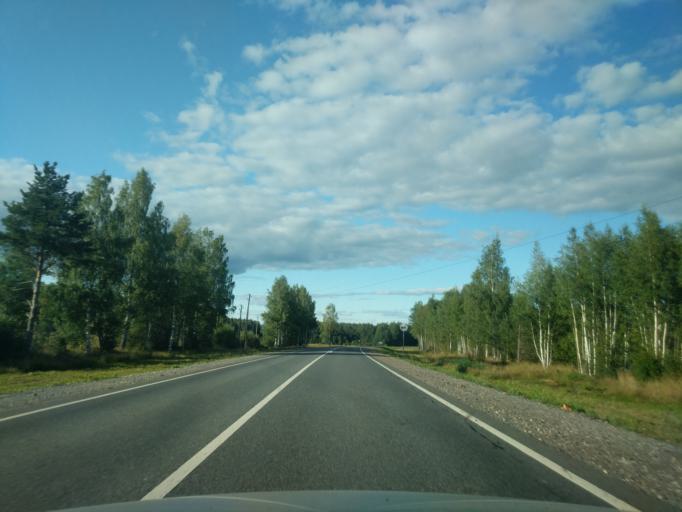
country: RU
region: Kostroma
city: Manturovo
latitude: 58.3378
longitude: 44.7164
